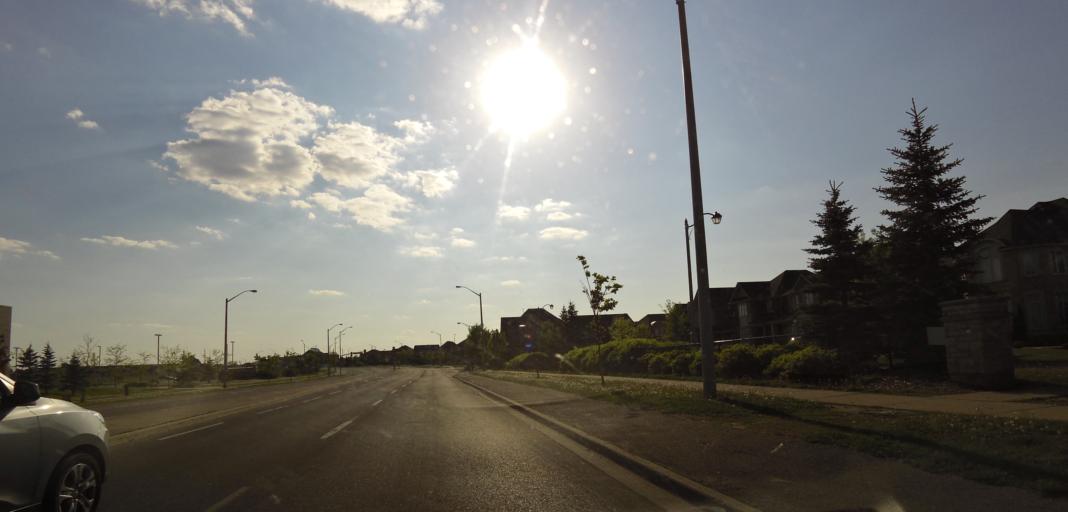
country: CA
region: Ontario
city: Brampton
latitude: 43.7667
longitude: -79.7440
